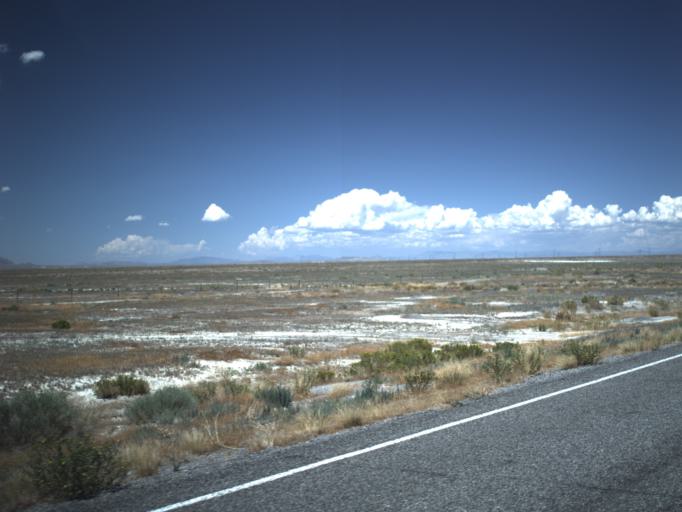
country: US
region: Utah
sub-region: Millard County
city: Delta
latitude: 39.2292
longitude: -112.9338
